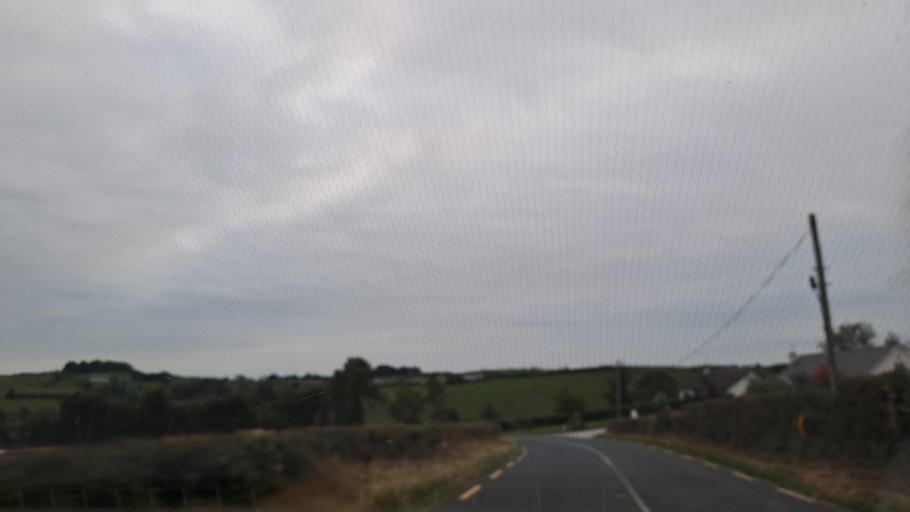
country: IE
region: Ulster
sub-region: County Monaghan
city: Carrickmacross
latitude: 54.0276
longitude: -6.7774
